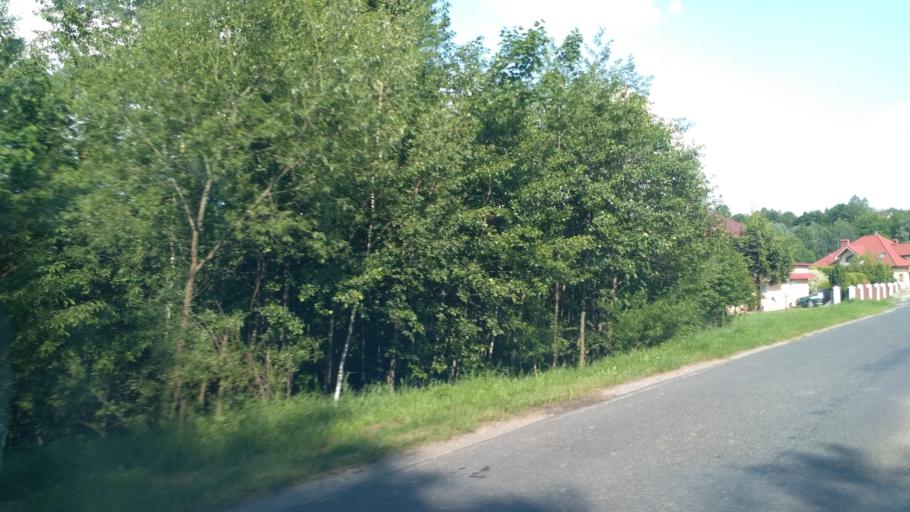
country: PL
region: Subcarpathian Voivodeship
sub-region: Powiat jaroslawski
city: Kramarzowka
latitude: 49.8743
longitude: 22.5086
